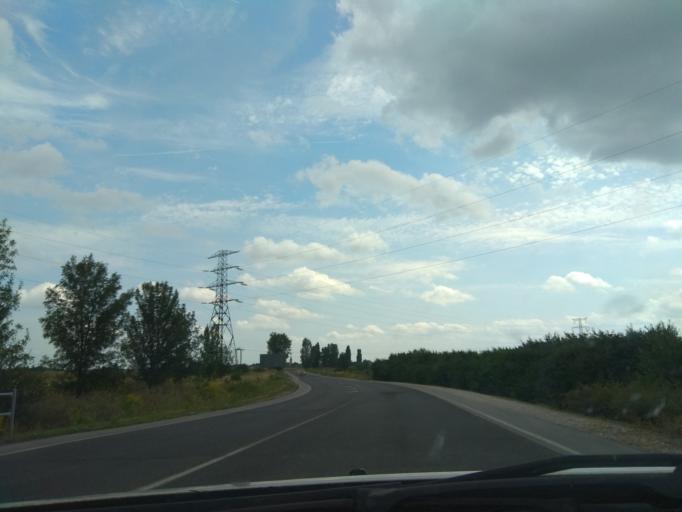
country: HU
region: Borsod-Abauj-Zemplen
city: Malyi
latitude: 48.0549
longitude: 20.8288
